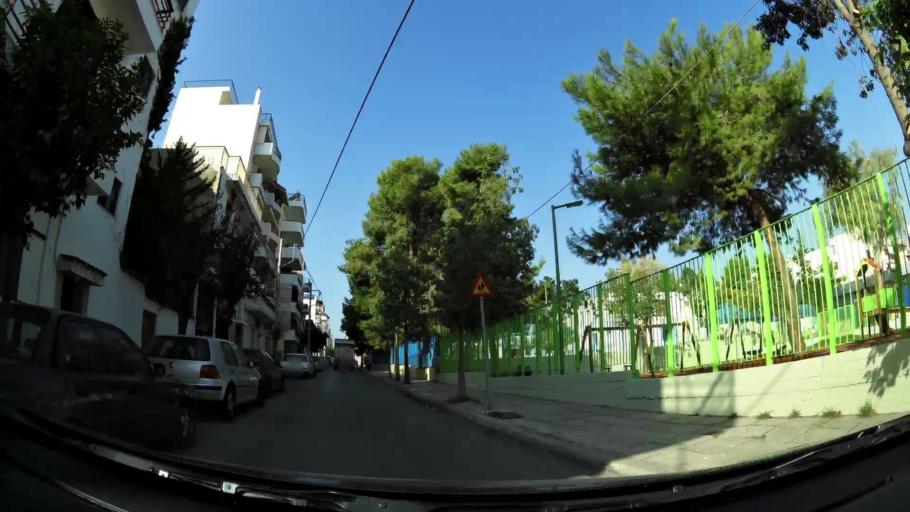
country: GR
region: Attica
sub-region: Nomos Piraios
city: Drapetsona
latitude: 37.9506
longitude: 23.6287
